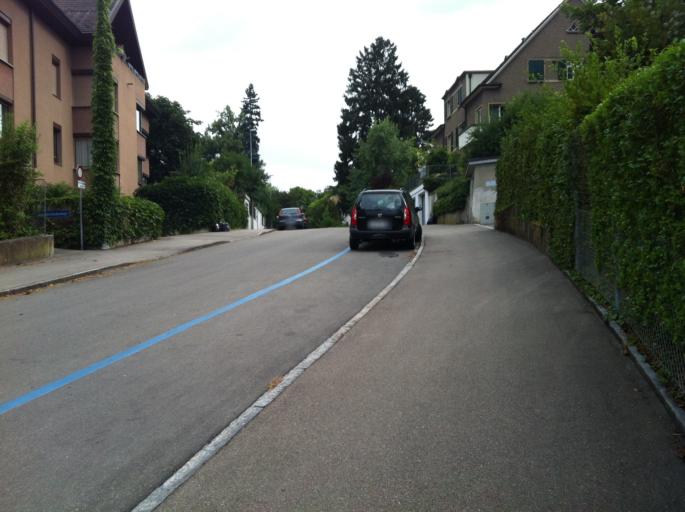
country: CH
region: Basel-City
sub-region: Basel-Stadt
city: Riehen
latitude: 47.5758
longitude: 7.6382
